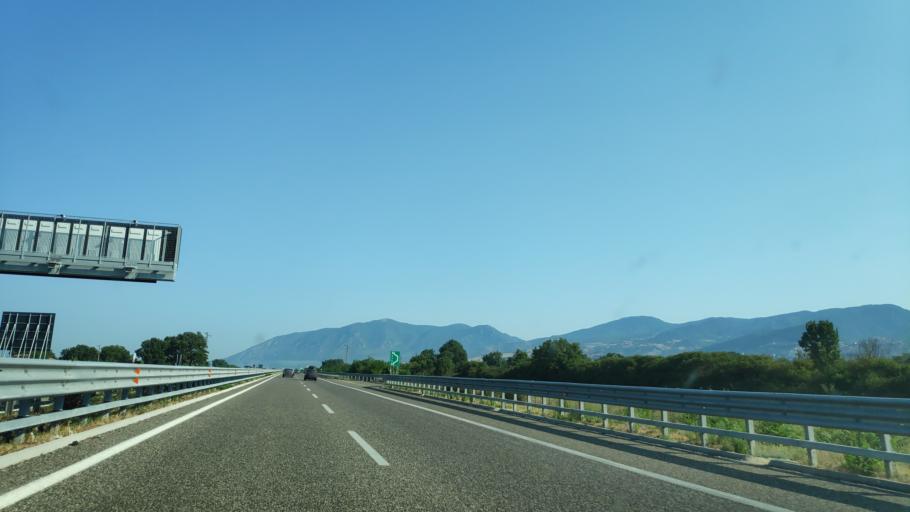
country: IT
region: Campania
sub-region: Provincia di Salerno
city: Padula
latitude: 40.3149
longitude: 15.6410
